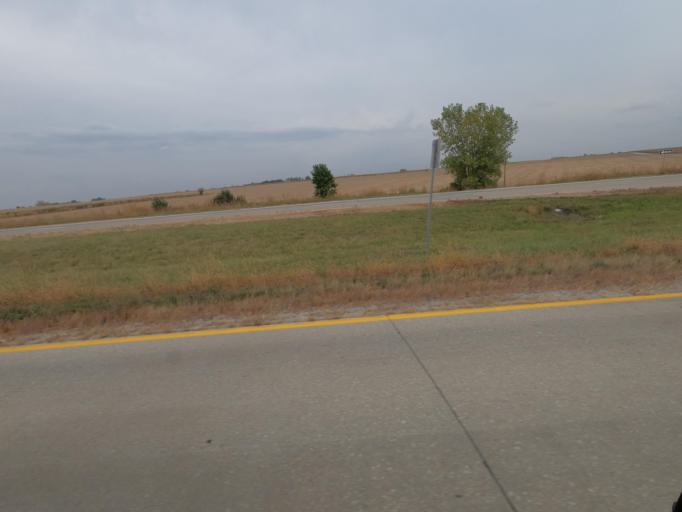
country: US
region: Iowa
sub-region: Marion County
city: Pella
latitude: 41.3800
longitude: -92.8194
